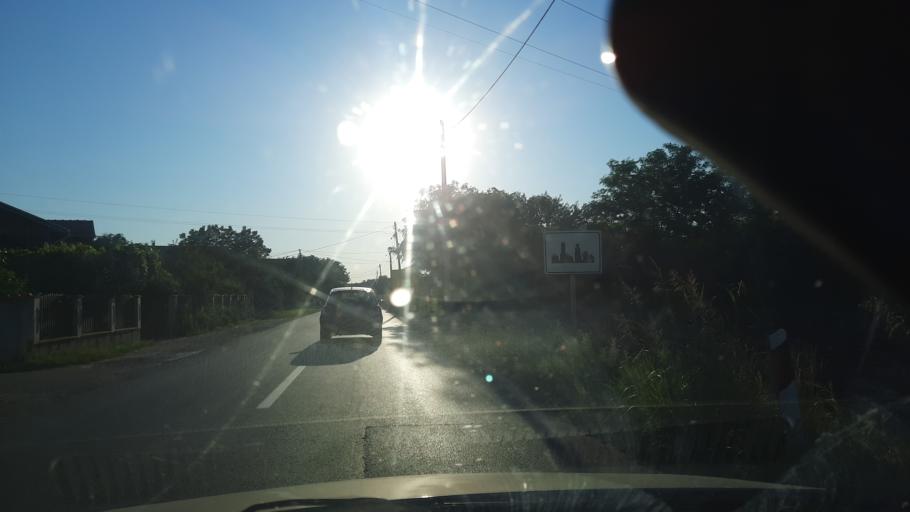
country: RS
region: Central Serbia
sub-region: Branicevski Okrug
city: Malo Crnice
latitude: 44.5871
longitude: 21.2805
